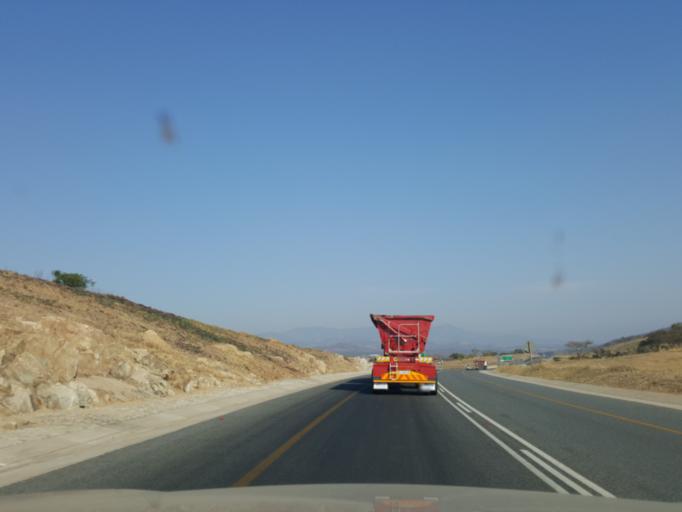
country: ZA
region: Mpumalanga
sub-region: Ehlanzeni District
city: Nelspruit
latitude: -25.4374
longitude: 30.9548
